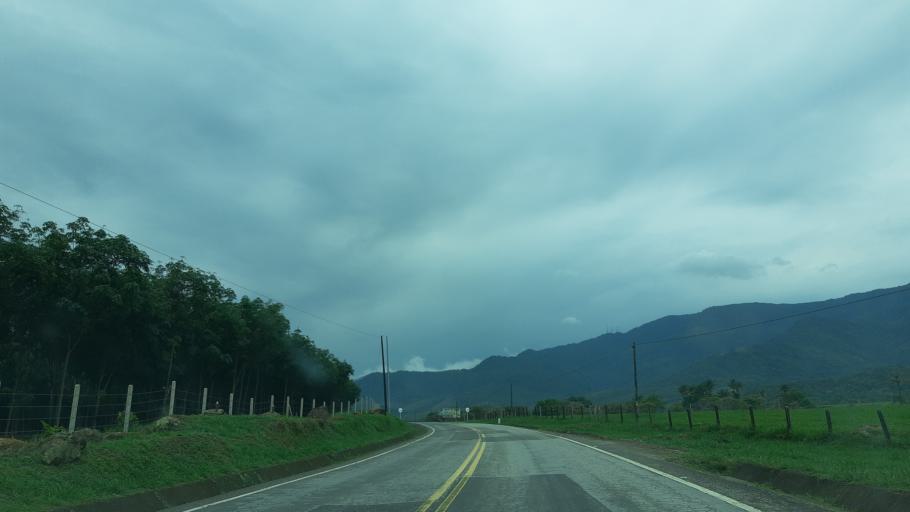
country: CO
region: Casanare
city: Monterrey
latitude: 4.8469
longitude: -72.9392
